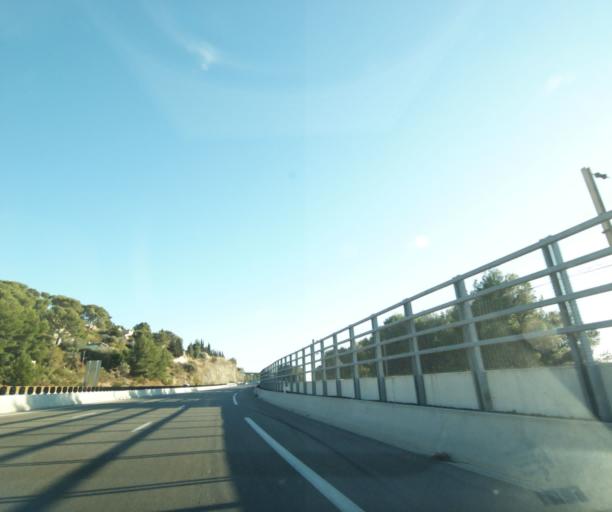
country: FR
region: Provence-Alpes-Cote d'Azur
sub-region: Departement des Bouches-du-Rhone
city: Ceyreste
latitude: 43.2066
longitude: 5.6312
